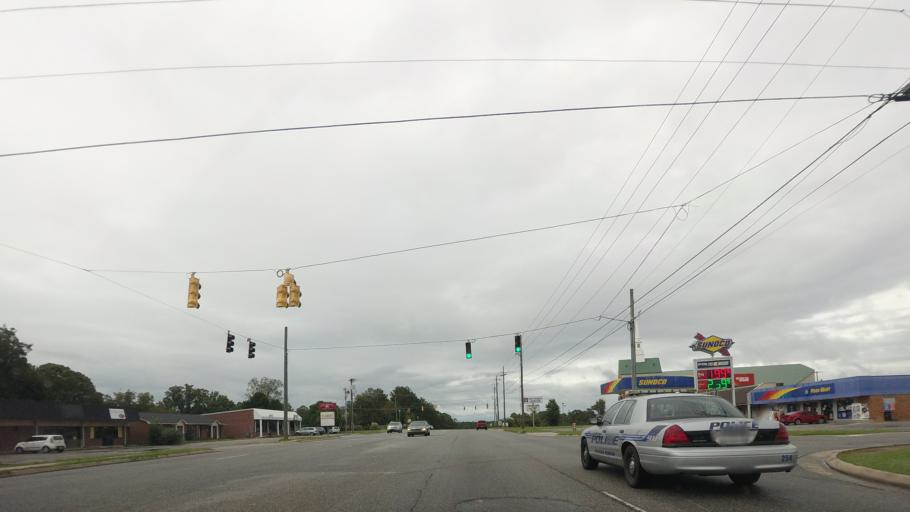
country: US
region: Georgia
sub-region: Houston County
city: Warner Robins
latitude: 32.5780
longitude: -83.6237
